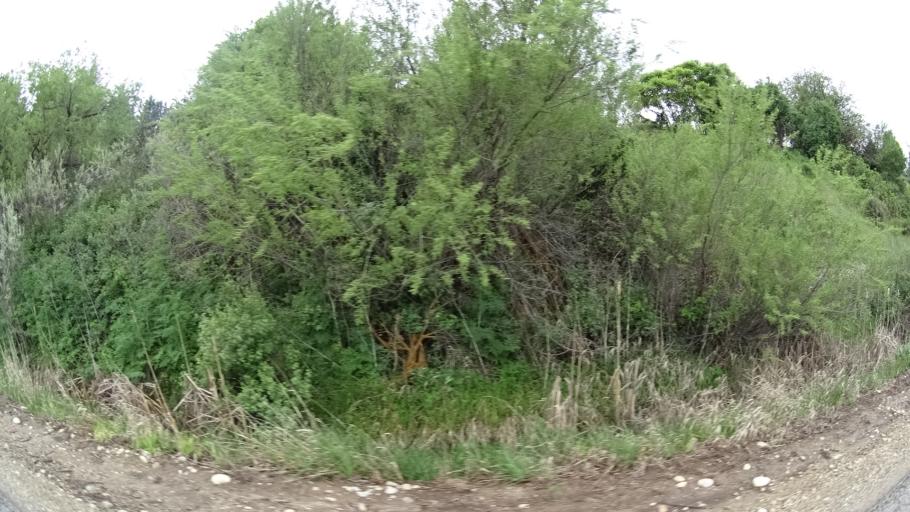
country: US
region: Idaho
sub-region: Ada County
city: Star
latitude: 43.6698
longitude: -116.4750
